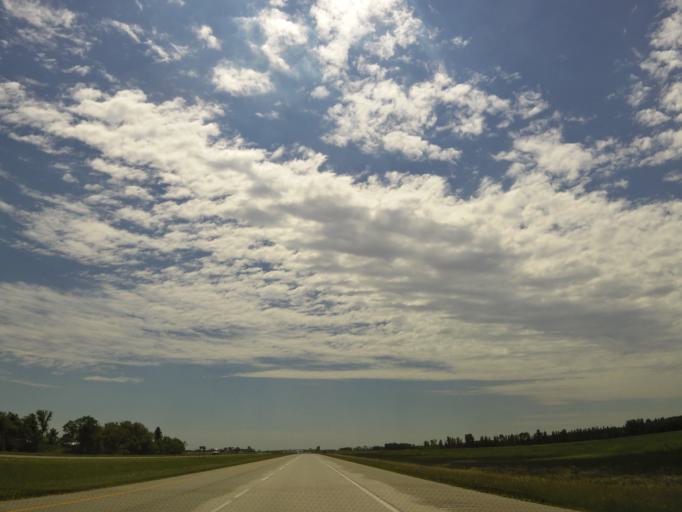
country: US
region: North Dakota
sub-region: Walsh County
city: Grafton
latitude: 48.3129
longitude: -97.1897
